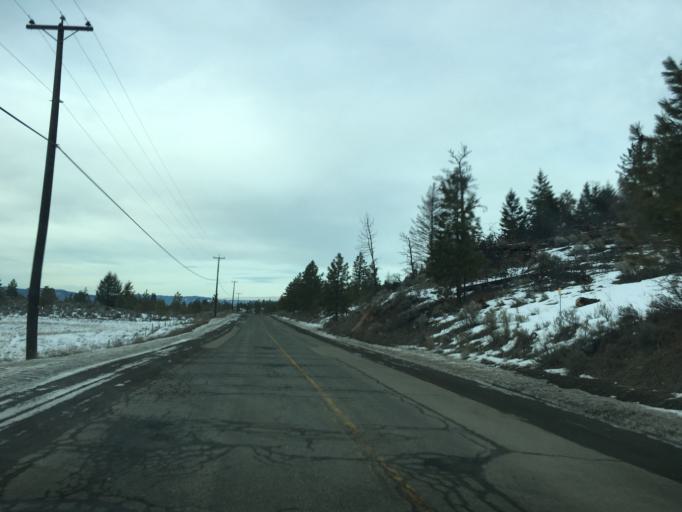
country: CA
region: British Columbia
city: Kamloops
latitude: 50.6437
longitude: -120.4498
